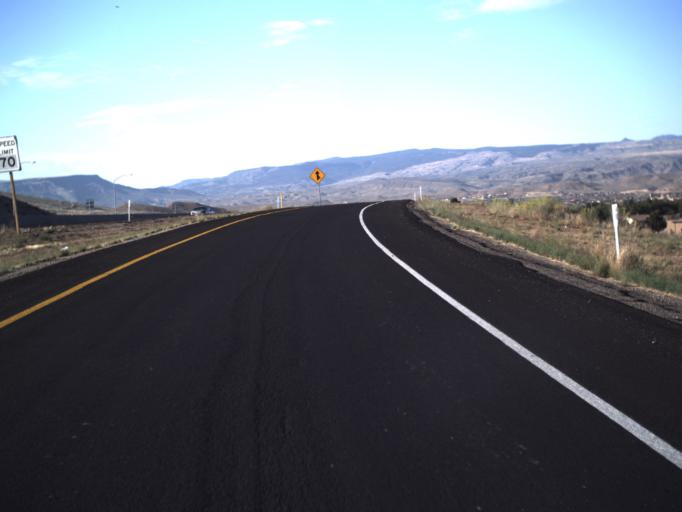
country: US
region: Utah
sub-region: Washington County
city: Saint George
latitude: 37.0583
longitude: -113.5860
